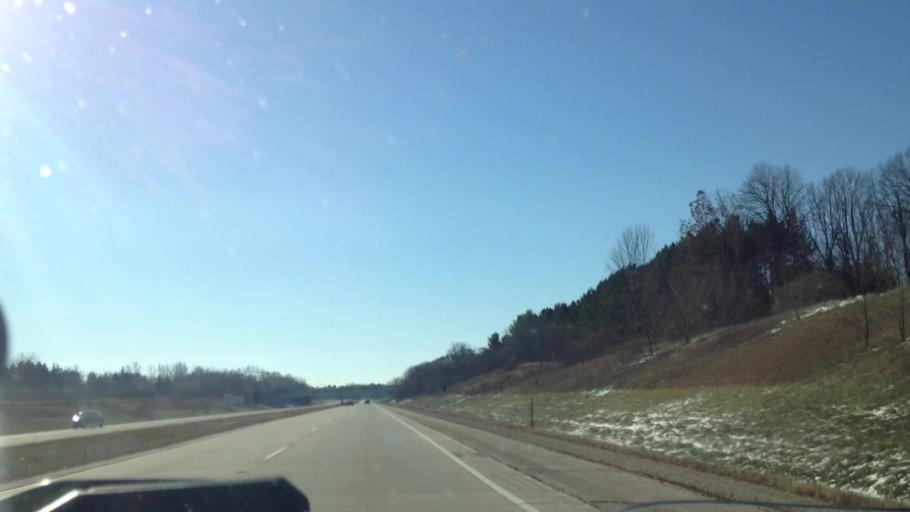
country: US
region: Wisconsin
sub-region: Washington County
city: West Bend
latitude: 43.3806
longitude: -88.1932
